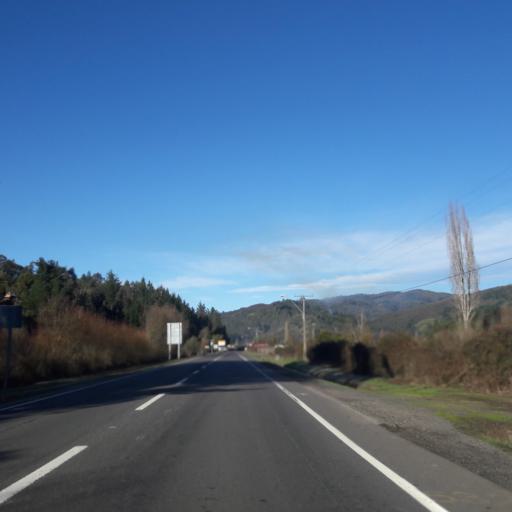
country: CL
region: Biobio
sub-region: Provincia de Concepcion
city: Lota
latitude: -37.2273
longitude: -72.9615
